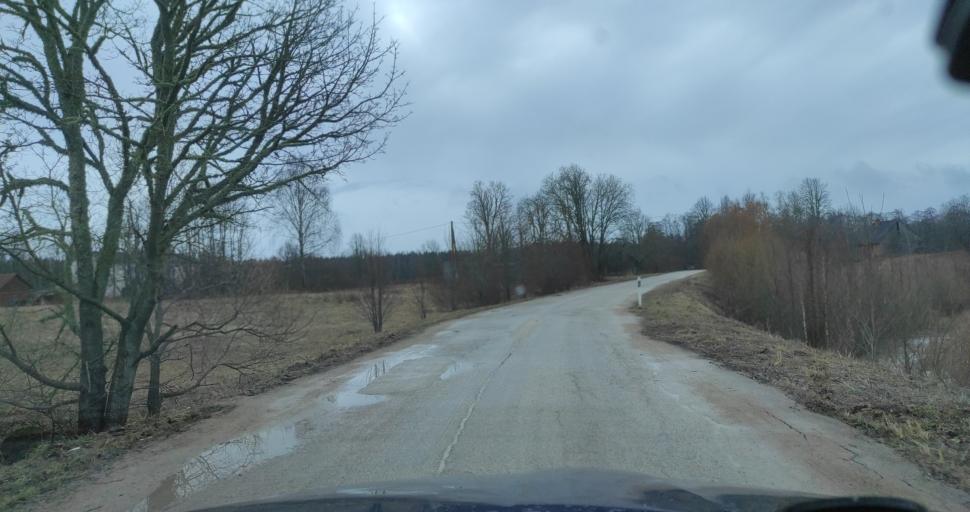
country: LV
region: Tukuma Rajons
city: Tukums
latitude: 57.0926
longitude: 23.0927
